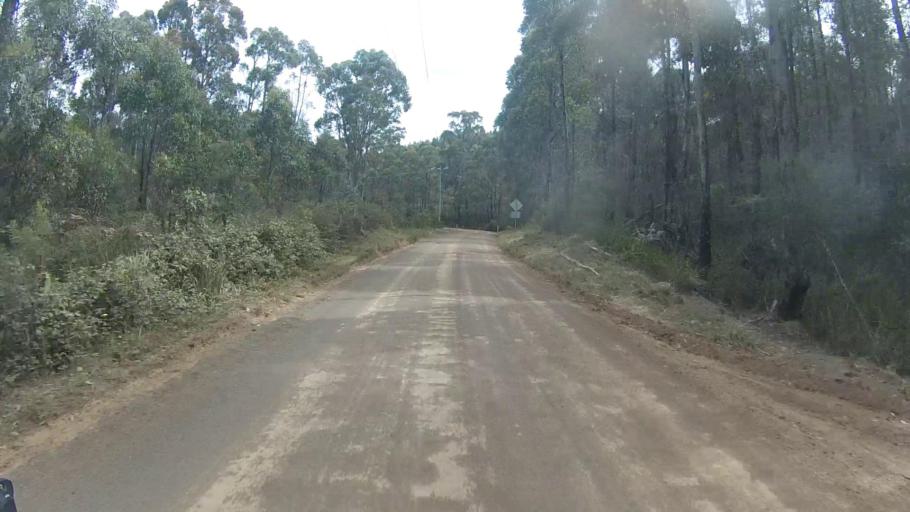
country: AU
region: Tasmania
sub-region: Sorell
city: Sorell
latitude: -42.7672
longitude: 147.8055
